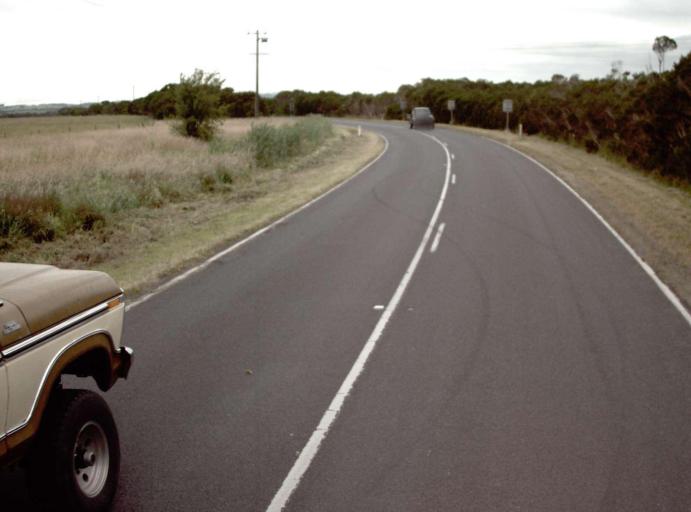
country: AU
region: Victoria
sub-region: Bass Coast
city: North Wonthaggi
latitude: -38.5924
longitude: 145.6121
